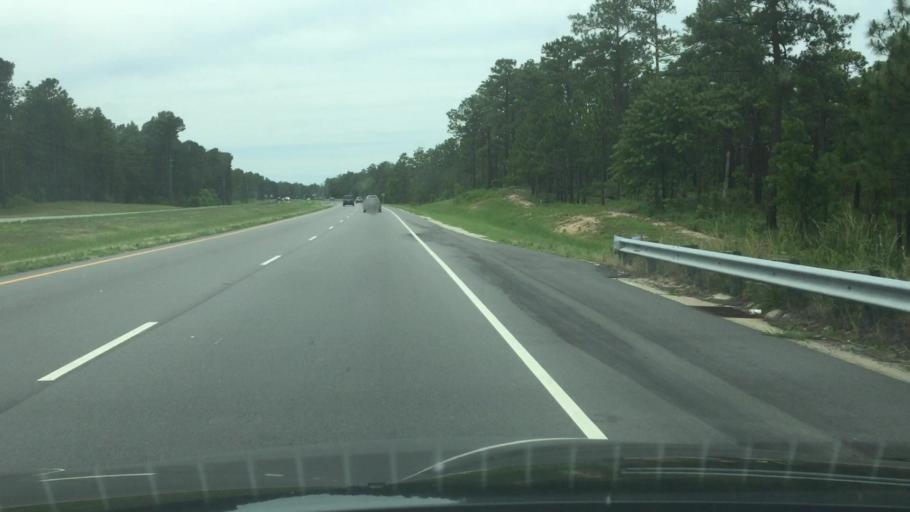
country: US
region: North Carolina
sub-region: Cumberland County
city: Spring Lake
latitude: 35.2259
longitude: -79.0098
